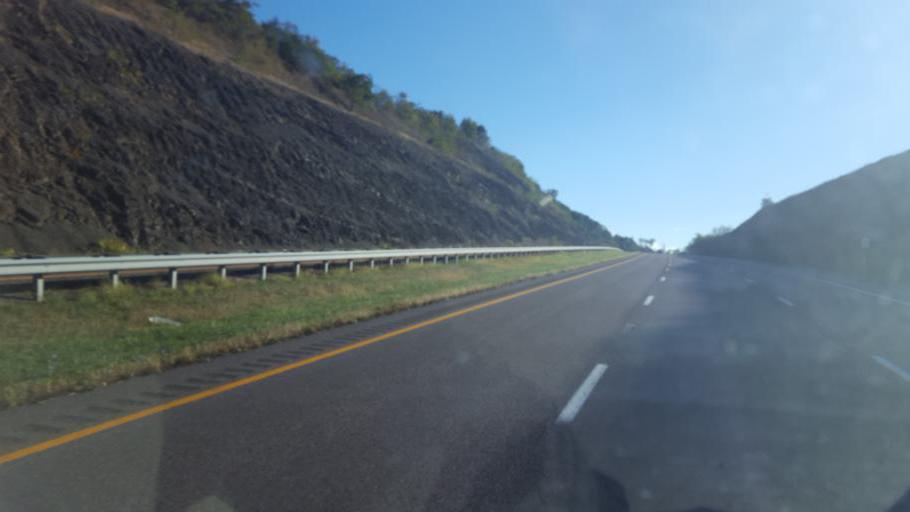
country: US
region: Maryland
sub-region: Allegany County
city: Cumberland
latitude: 39.6950
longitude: -78.5275
